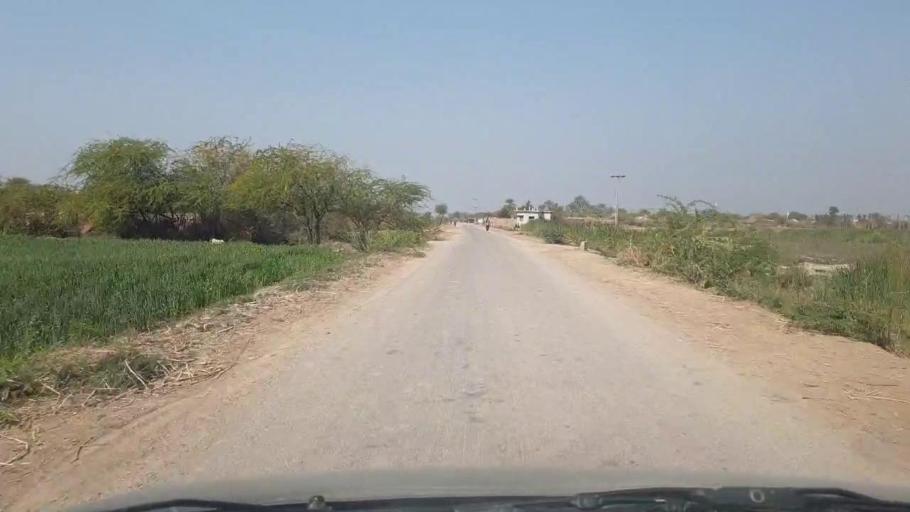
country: PK
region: Sindh
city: Mirwah Gorchani
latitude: 25.3265
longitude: 69.1495
